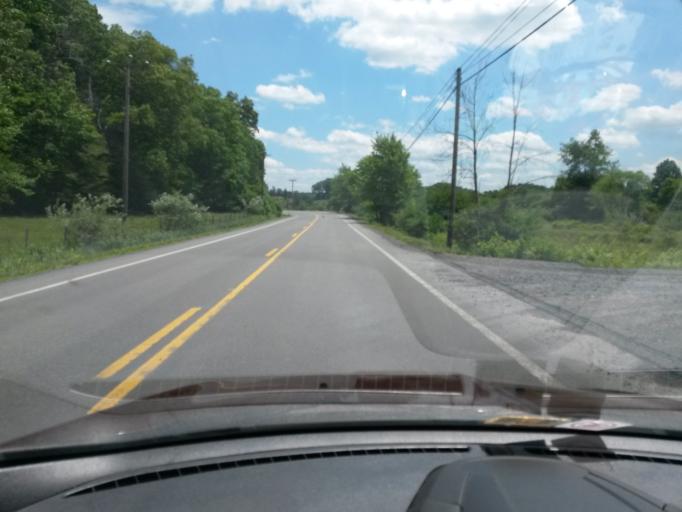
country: US
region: West Virginia
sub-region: Greenbrier County
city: Rainelle
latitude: 37.9469
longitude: -80.6551
